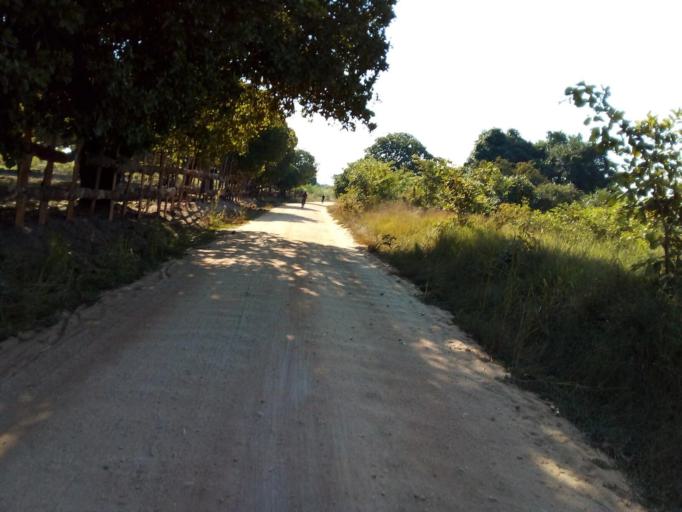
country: MZ
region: Zambezia
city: Quelimane
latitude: -17.5375
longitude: 36.6232
